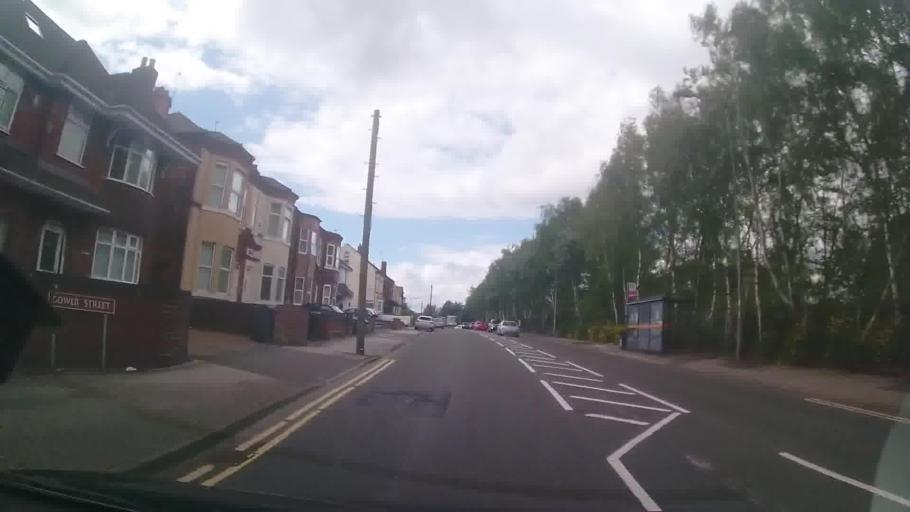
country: GB
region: England
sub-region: Walsall
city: Walsall
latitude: 52.5752
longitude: -2.0055
